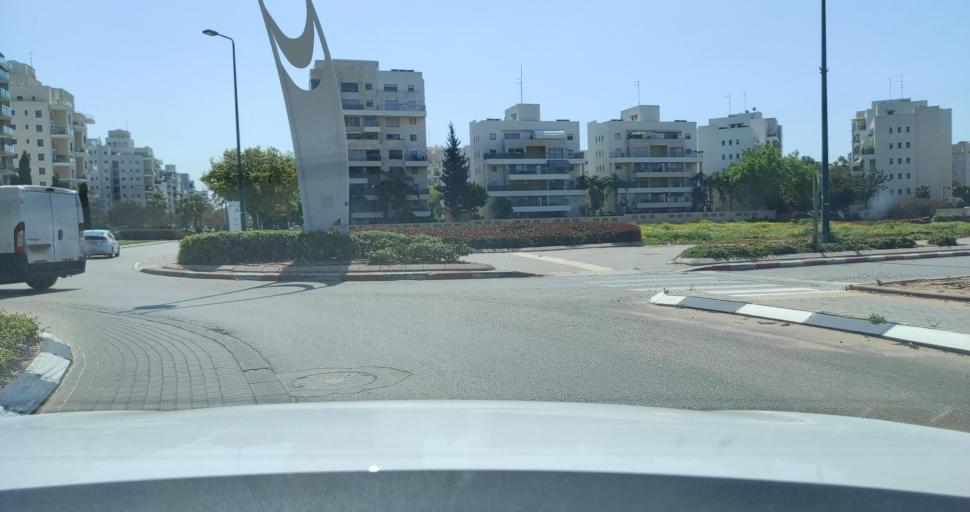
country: IL
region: Central District
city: Nordiyya
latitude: 32.3034
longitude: 34.8737
